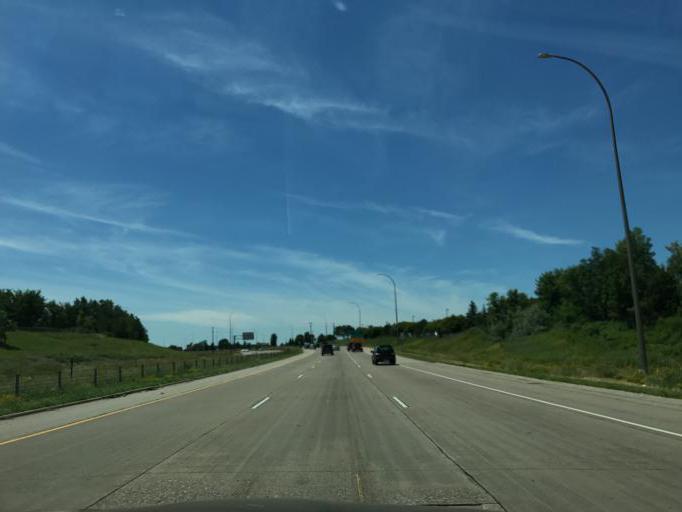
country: US
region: Minnesota
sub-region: Hennepin County
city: Osseo
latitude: 45.1037
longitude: -93.3969
